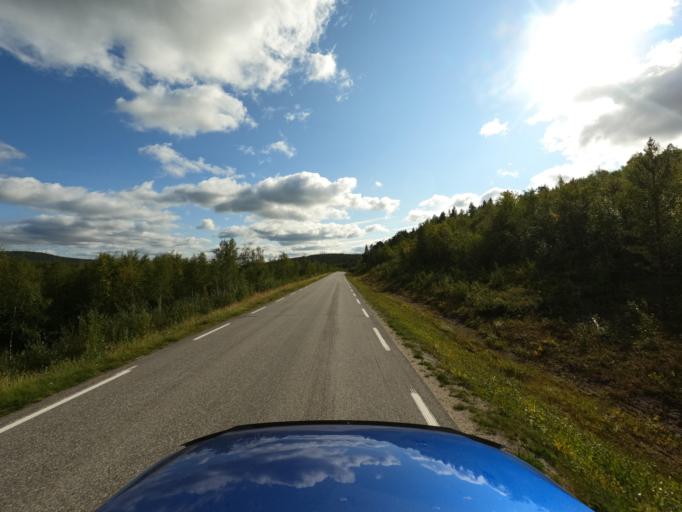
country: NO
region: Finnmark Fylke
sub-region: Karasjok
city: Karasjohka
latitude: 69.4526
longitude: 25.5783
